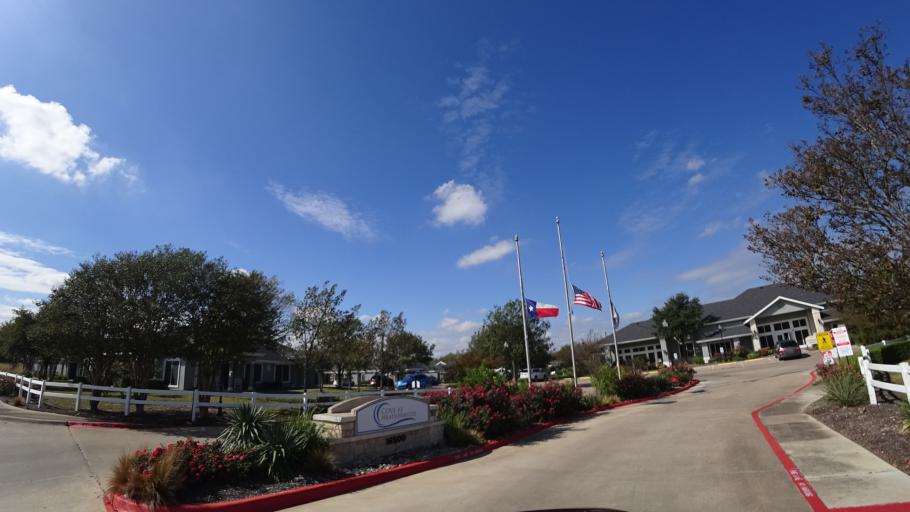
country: US
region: Texas
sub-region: Travis County
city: Windemere
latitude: 30.4532
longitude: -97.6381
